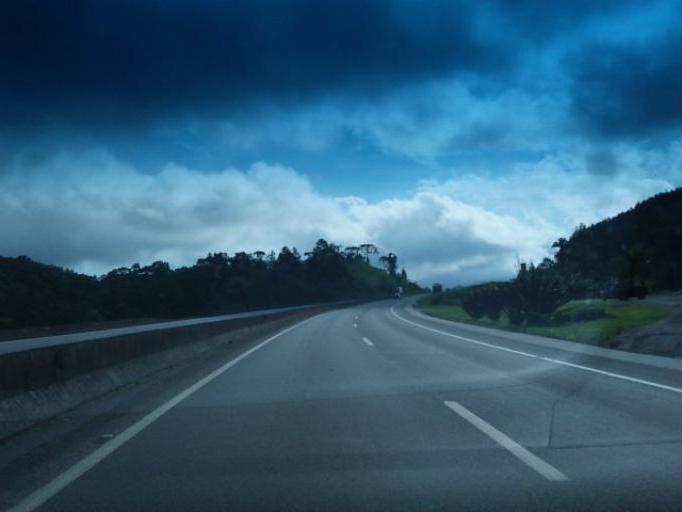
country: BR
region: Parana
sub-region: Antonina
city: Antonina
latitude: -25.1067
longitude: -48.7409
